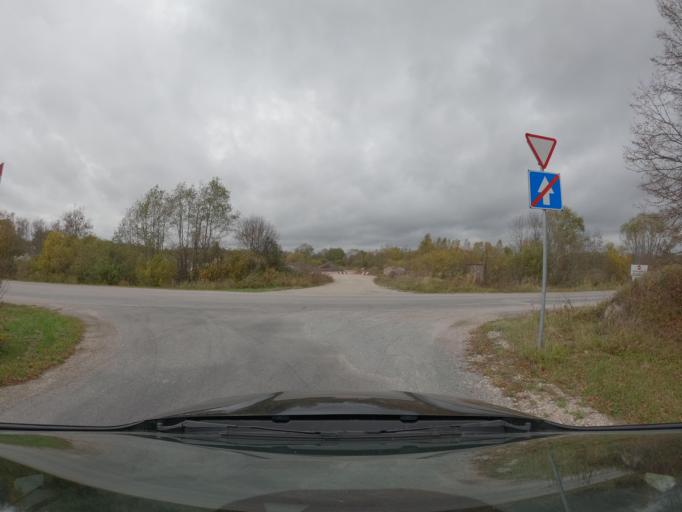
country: EE
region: Saare
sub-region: Kuressaare linn
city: Kuressaare
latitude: 58.2696
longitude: 22.4846
